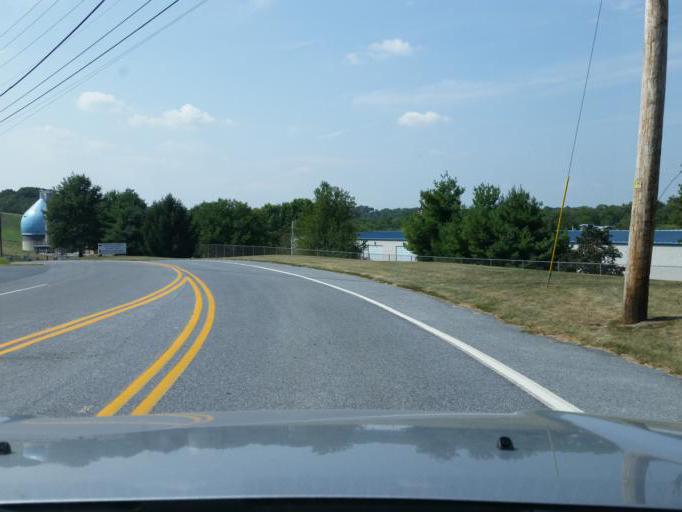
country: US
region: Pennsylvania
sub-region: Dauphin County
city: Hershey
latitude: 40.2833
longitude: -76.6819
